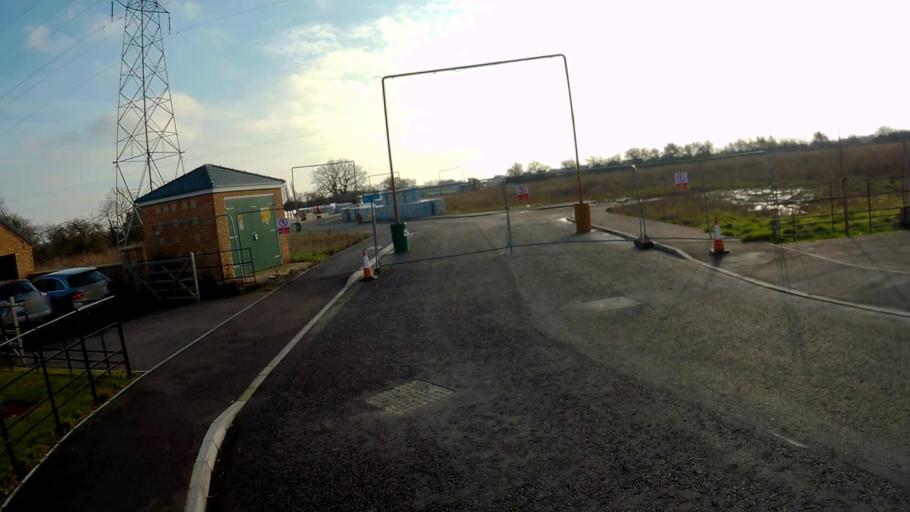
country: GB
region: England
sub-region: Lincolnshire
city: Bourne
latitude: 52.7643
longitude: -0.3933
